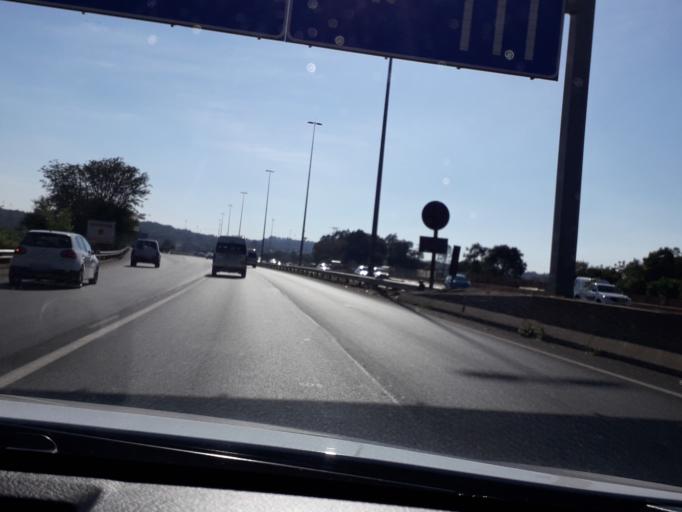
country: ZA
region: Gauteng
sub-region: City of Tshwane Metropolitan Municipality
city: Pretoria
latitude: -25.7415
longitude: 28.2566
